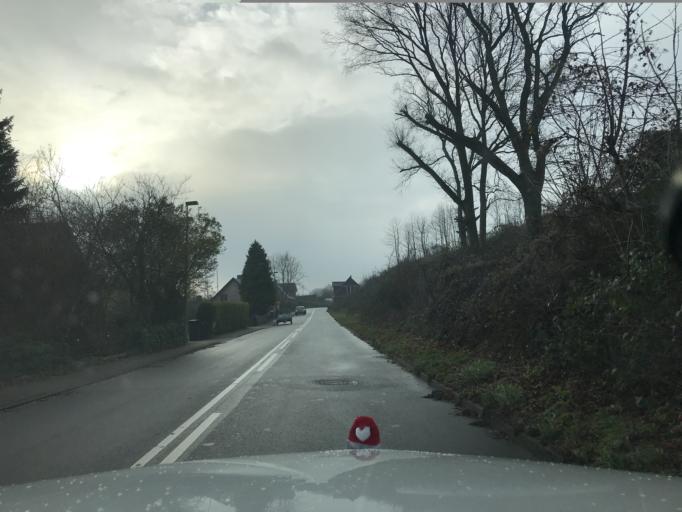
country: DK
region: South Denmark
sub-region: Sonderborg Kommune
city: Grasten
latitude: 54.8978
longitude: 9.5660
